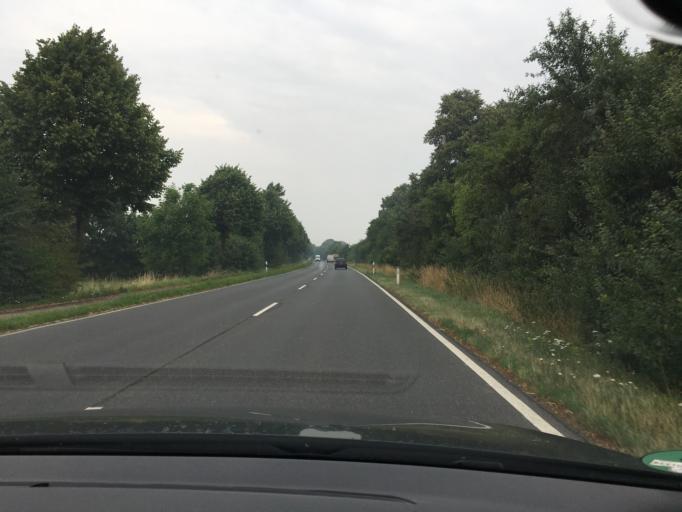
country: DE
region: North Rhine-Westphalia
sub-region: Regierungsbezirk Koln
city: Titz
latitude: 50.9467
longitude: 6.4212
